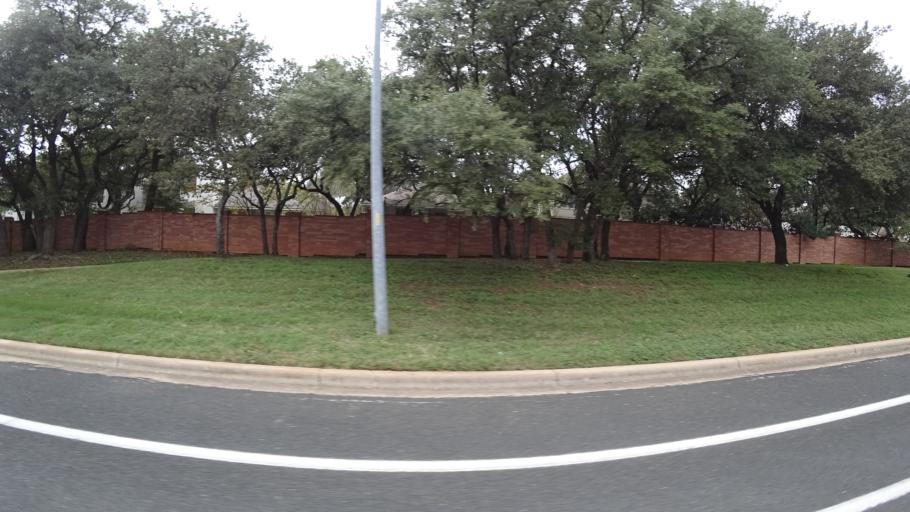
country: US
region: Texas
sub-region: Travis County
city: Shady Hollow
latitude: 30.2190
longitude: -97.8738
